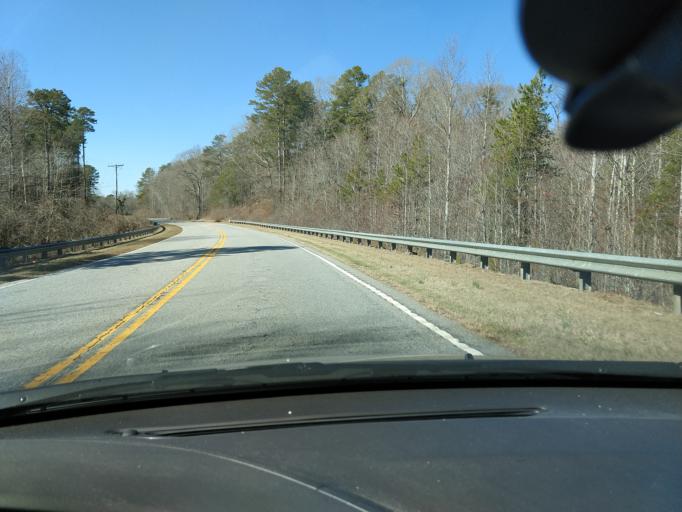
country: US
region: South Carolina
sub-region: Oconee County
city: Westminster
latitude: 34.6132
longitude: -83.1582
